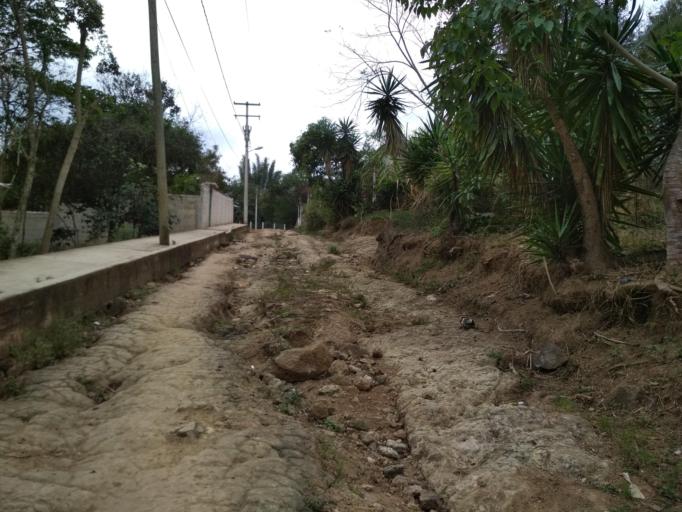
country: MX
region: Veracruz
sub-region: Coatepec
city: Tuzamapan
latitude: 19.3674
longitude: -96.8810
